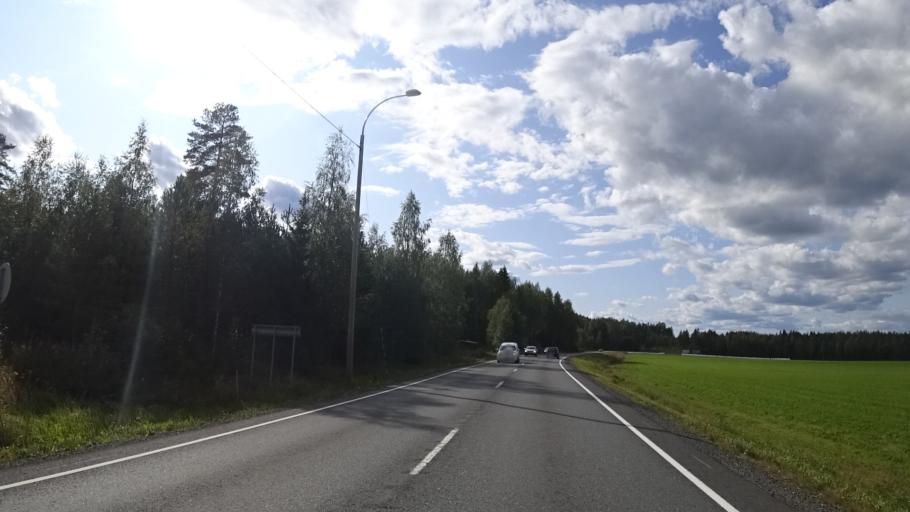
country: FI
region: North Karelia
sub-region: Keski-Karjala
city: Tohmajaervi
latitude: 62.1901
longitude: 30.4417
